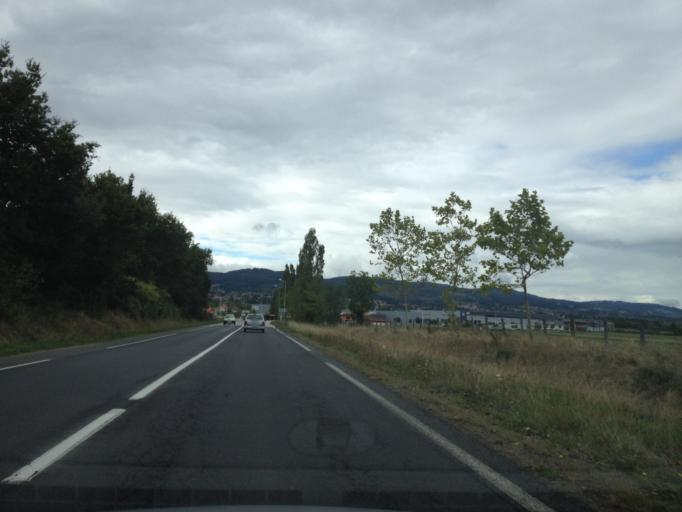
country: FR
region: Rhone-Alpes
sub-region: Departement de la Loire
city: Pouilly-les-Nonains
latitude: 46.0510
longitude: 3.9557
